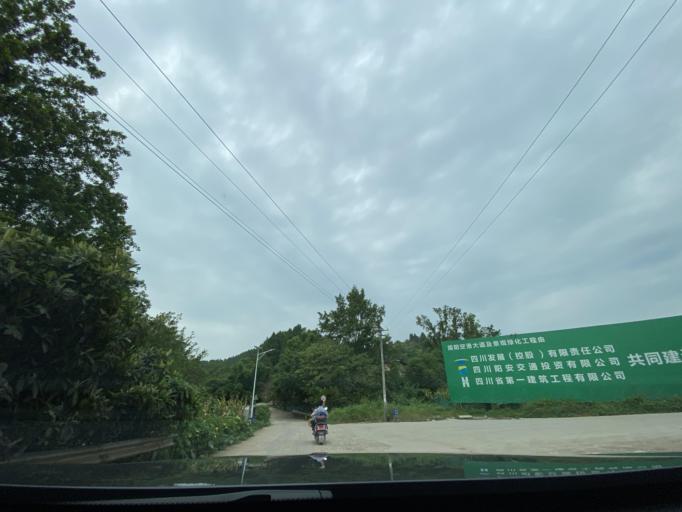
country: CN
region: Sichuan
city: Jiancheng
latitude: 30.3882
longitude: 104.5145
